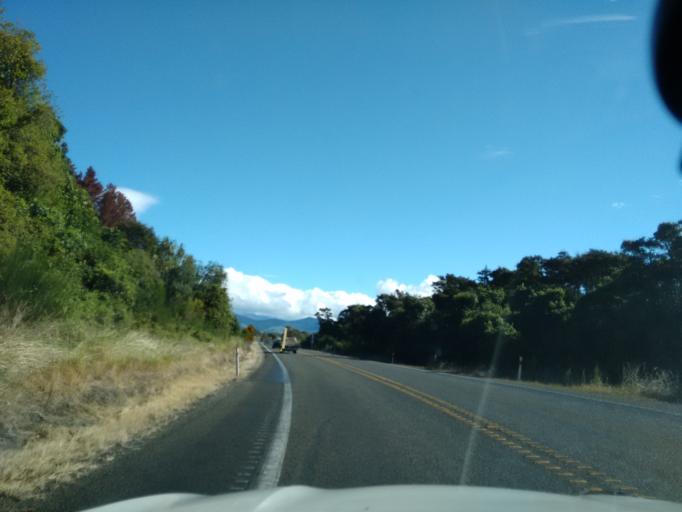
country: NZ
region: Waikato
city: Turangi
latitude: -38.9378
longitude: 175.8610
